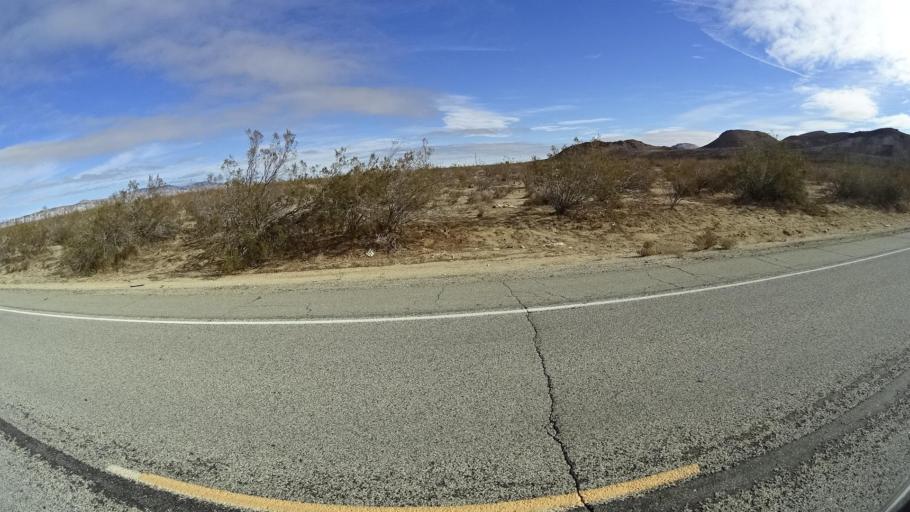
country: US
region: California
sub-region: Kern County
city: Mojave
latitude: 34.9672
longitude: -118.3008
